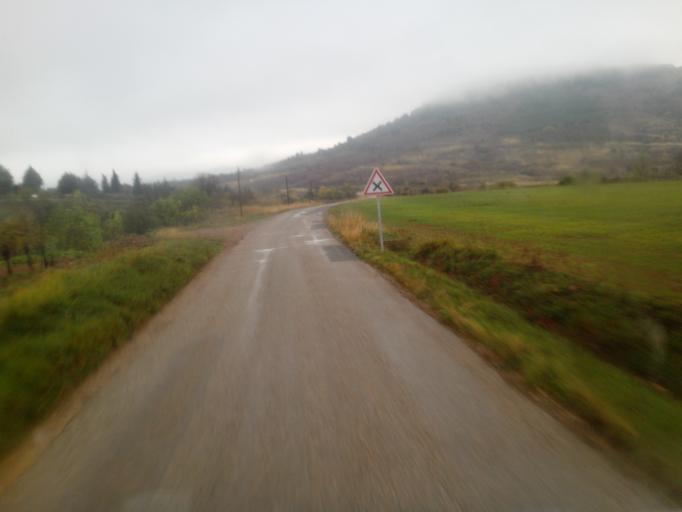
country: FR
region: Languedoc-Roussillon
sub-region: Departement de l'Herault
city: Lodeve
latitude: 43.6452
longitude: 3.3521
